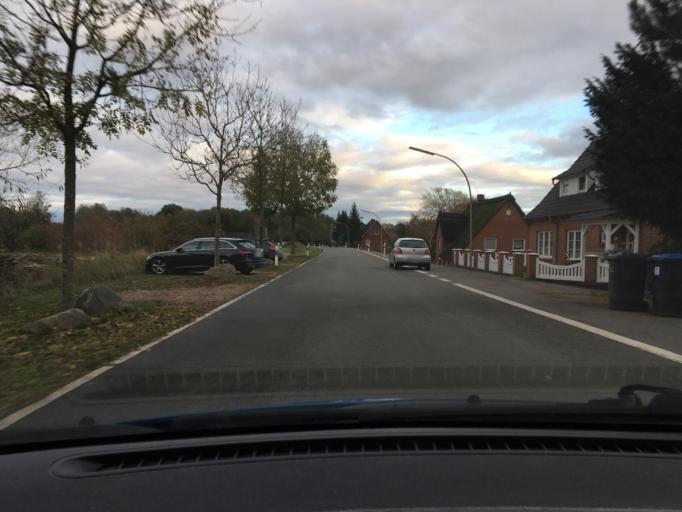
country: DE
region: Hamburg
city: Harburg
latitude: 53.4688
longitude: 10.0150
